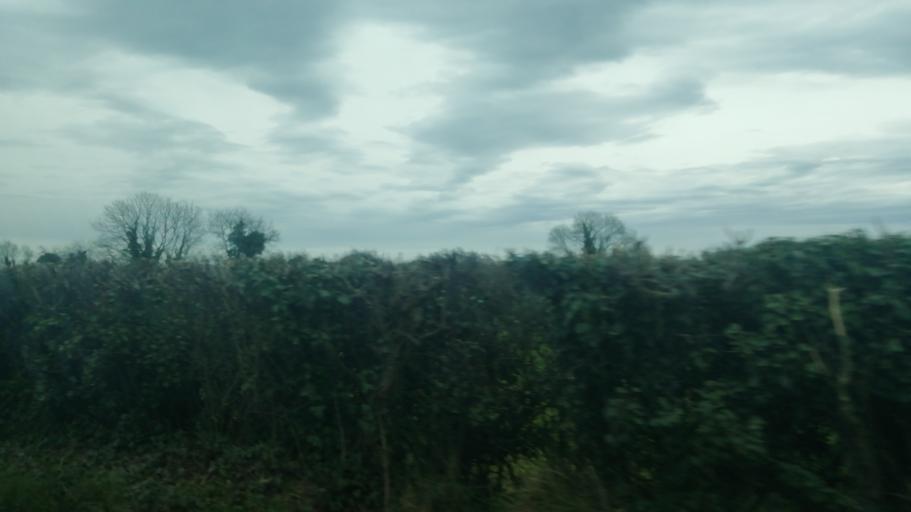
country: IE
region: Leinster
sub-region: Kildare
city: Clane
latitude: 53.3025
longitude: -6.6692
